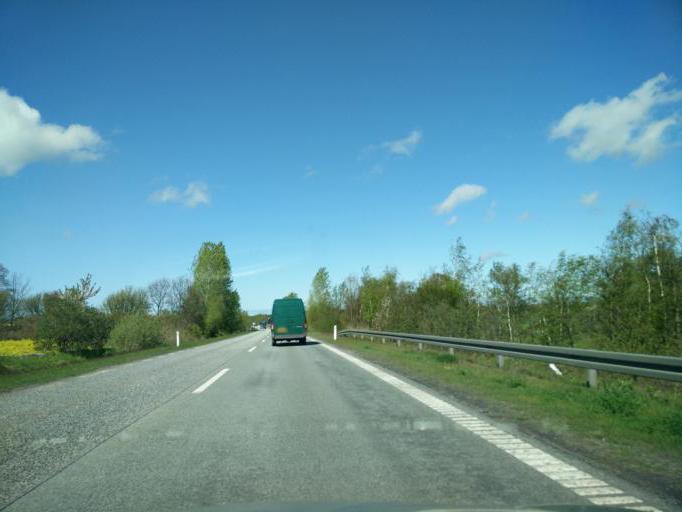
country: DK
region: Capital Region
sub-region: Gribskov Kommune
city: Helsinge
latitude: 55.9738
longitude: 12.2448
